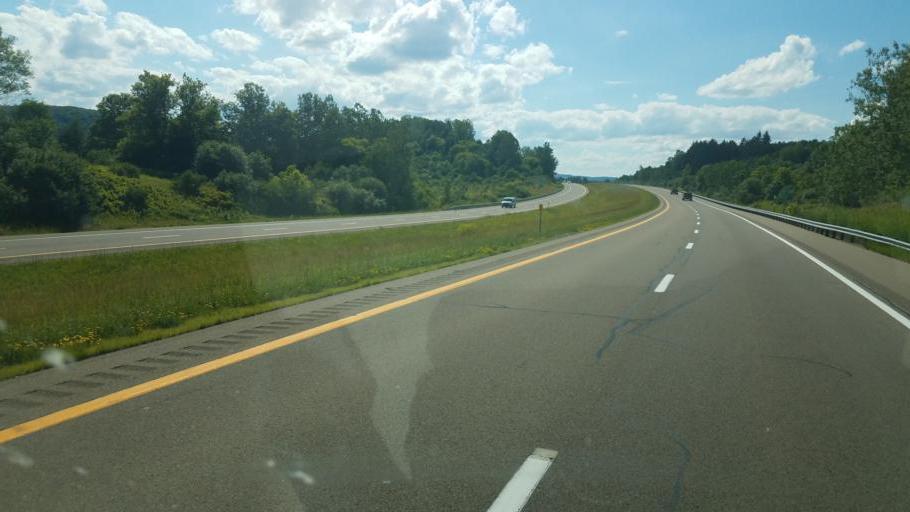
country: US
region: New York
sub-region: Steuben County
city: Hornell
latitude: 42.3734
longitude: -77.6313
